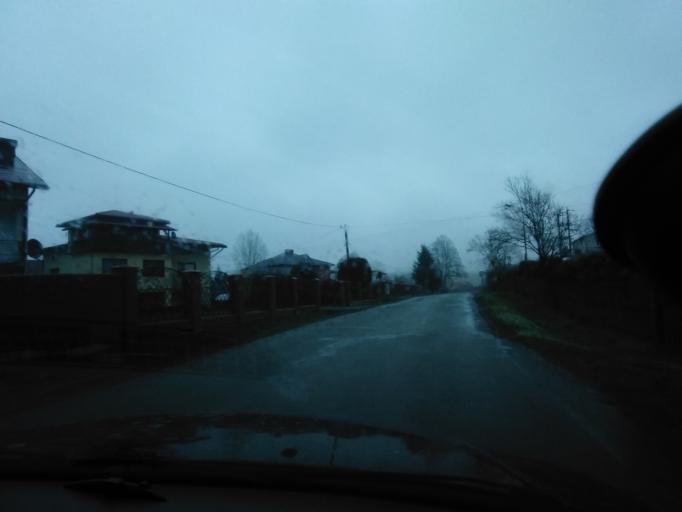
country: PL
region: Subcarpathian Voivodeship
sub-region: Powiat brzozowski
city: Jablonka
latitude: 49.7369
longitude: 22.0939
